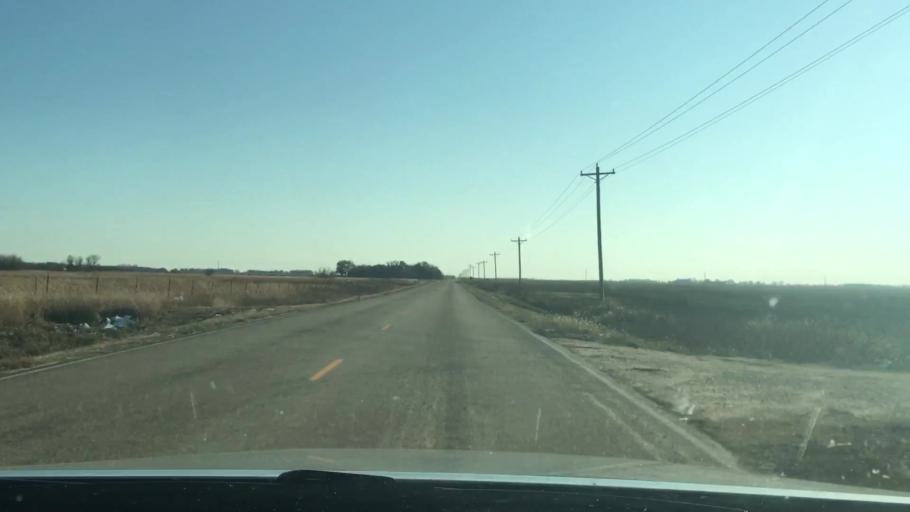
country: US
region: Kansas
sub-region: Reno County
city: Nickerson
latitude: 38.2366
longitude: -98.0877
